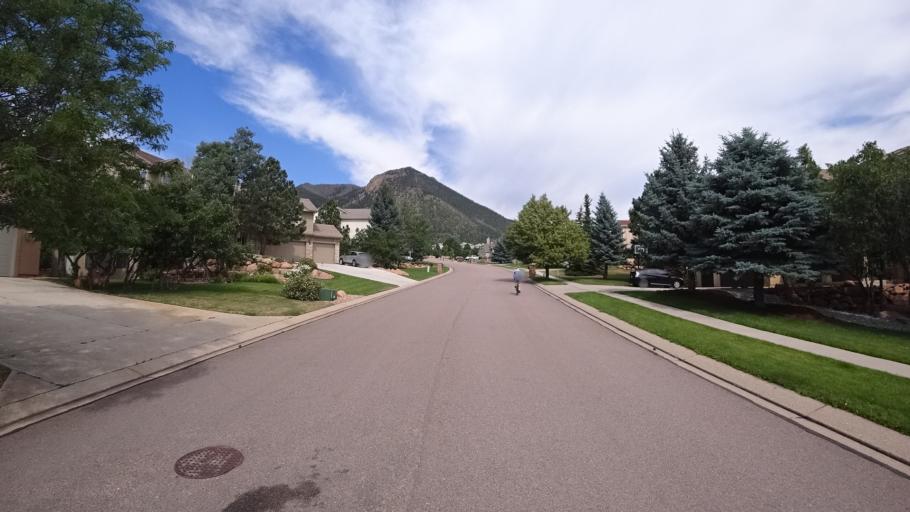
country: US
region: Colorado
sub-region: El Paso County
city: Air Force Academy
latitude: 38.9528
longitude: -104.8835
